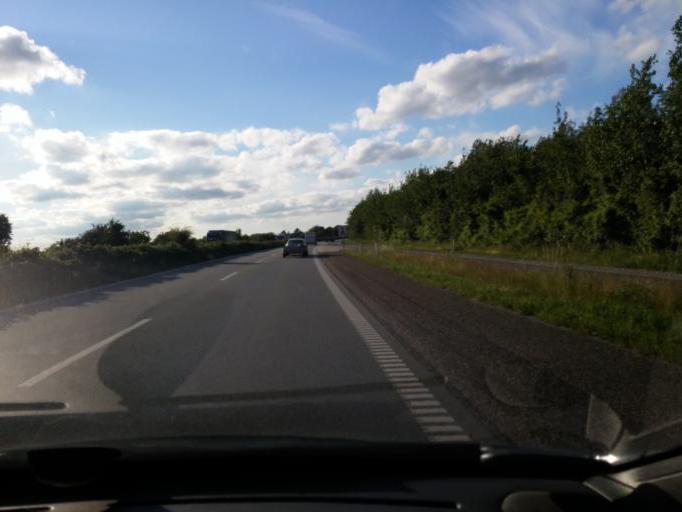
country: DK
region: South Denmark
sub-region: Nyborg Kommune
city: Nyborg
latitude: 55.3103
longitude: 10.8104
